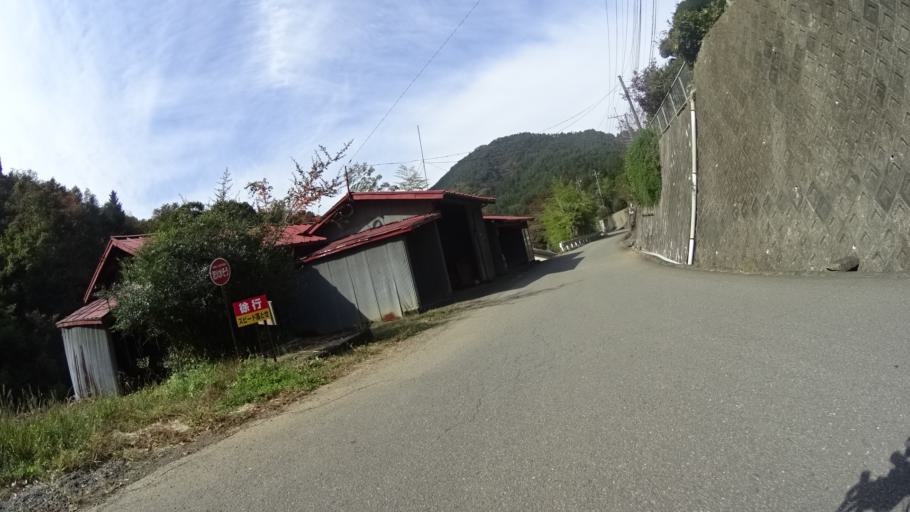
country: JP
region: Yamanashi
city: Otsuki
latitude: 35.5706
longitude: 138.9912
